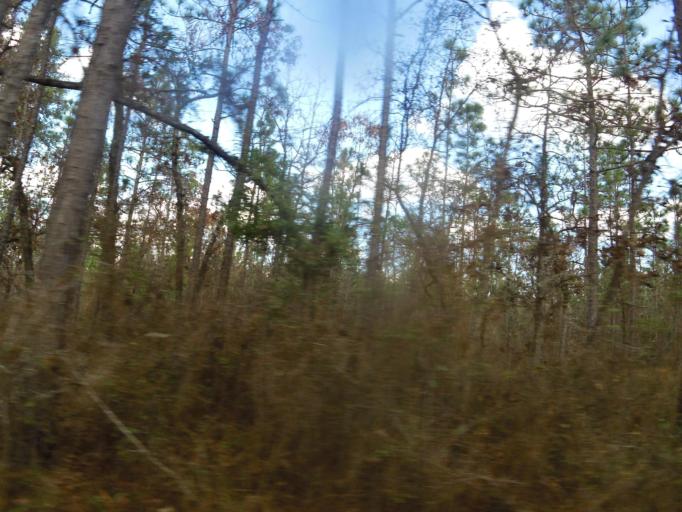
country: US
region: Florida
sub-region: Clay County
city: Middleburg
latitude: 30.1480
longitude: -81.9592
